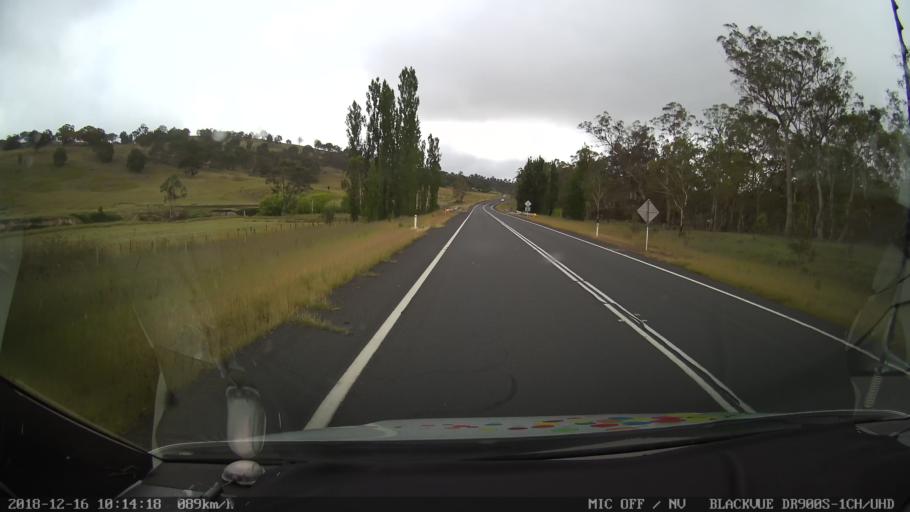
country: AU
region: New South Wales
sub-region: Tenterfield Municipality
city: Carrolls Creek
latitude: -29.2885
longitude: 151.9617
